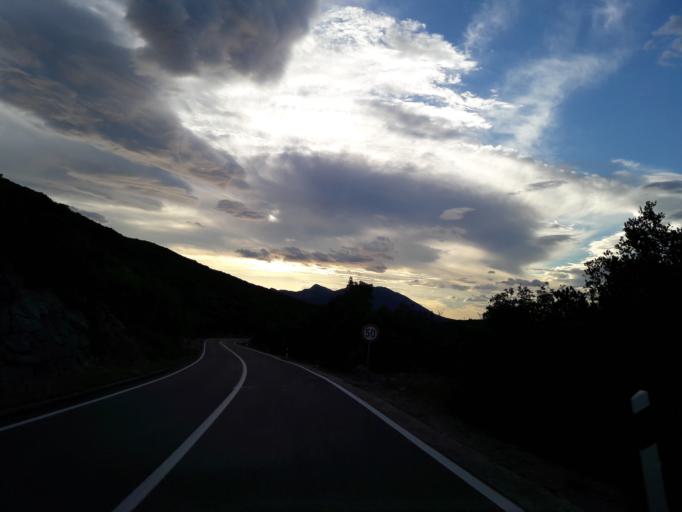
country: BA
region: Federation of Bosnia and Herzegovina
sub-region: Hercegovacko-Bosanski Kanton
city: Neum
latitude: 42.9030
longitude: 17.4843
